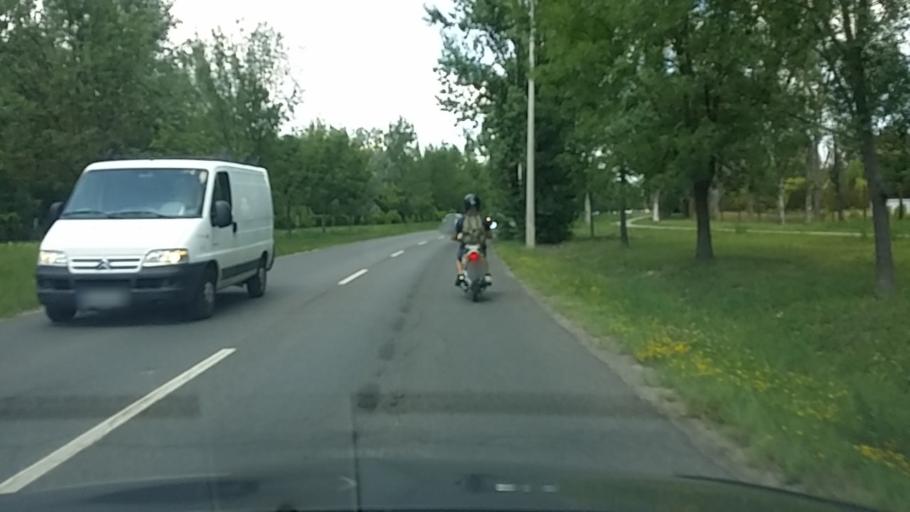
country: HU
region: Bacs-Kiskun
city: Kecskemet
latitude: 46.9120
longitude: 19.6542
